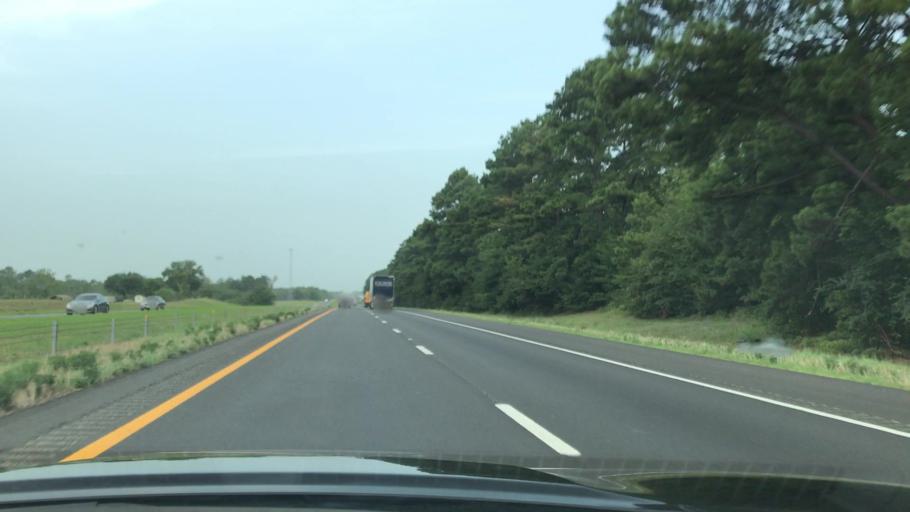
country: US
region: Texas
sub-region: Harrison County
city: Hallsville
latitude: 32.4658
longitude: -94.6291
